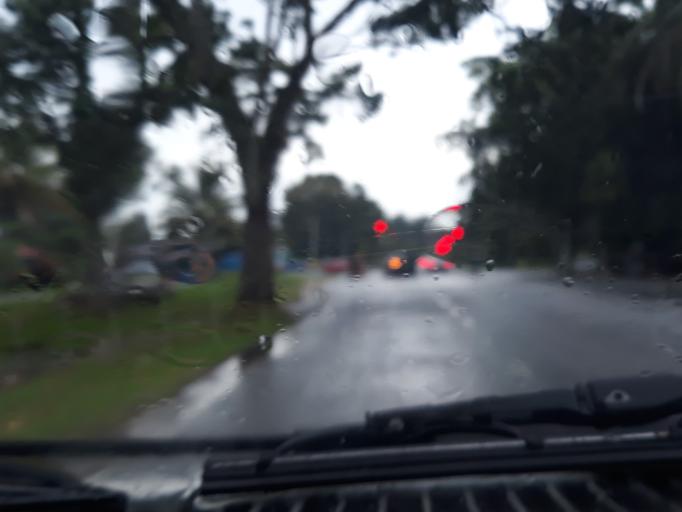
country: MY
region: Kedah
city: Kulim
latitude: 5.3717
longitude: 100.5813
